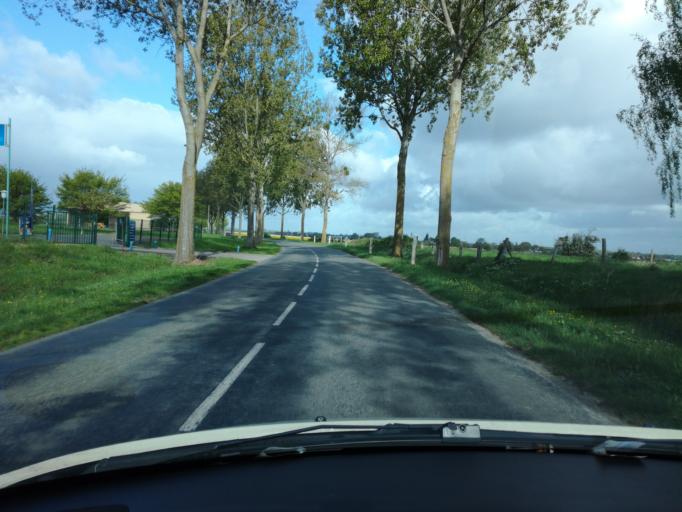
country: FR
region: Picardie
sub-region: Departement de la Somme
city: Hornoy-le-Bourg
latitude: 49.8505
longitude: 1.8932
